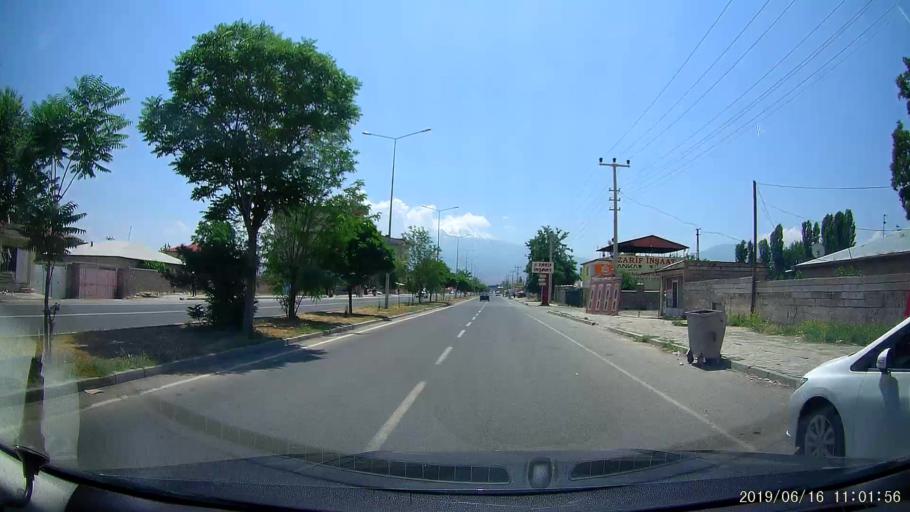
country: TR
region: Igdir
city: Igdir
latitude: 39.9112
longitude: 44.0550
